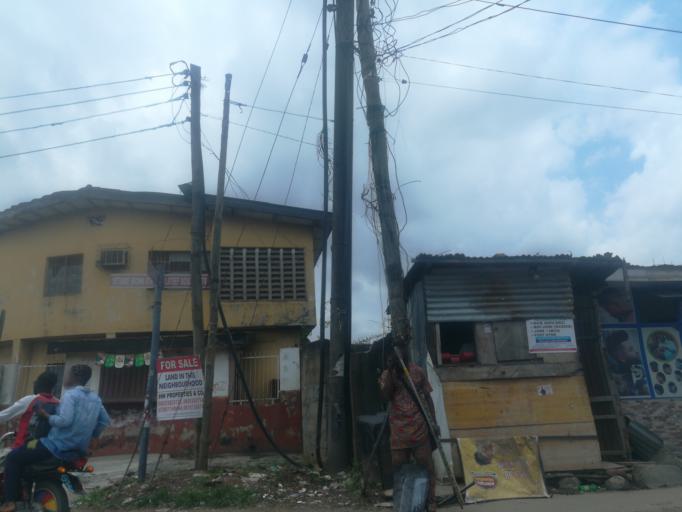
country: NG
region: Lagos
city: Ojota
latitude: 6.5628
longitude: 3.3917
